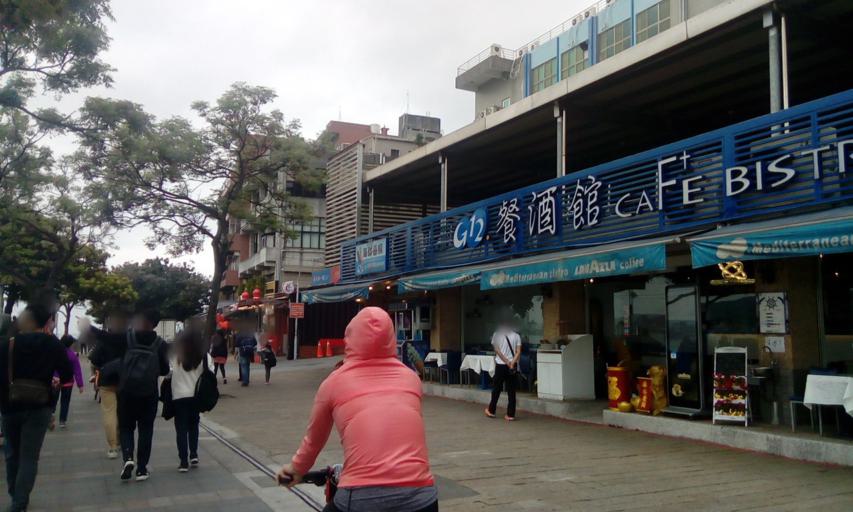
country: TW
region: Taipei
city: Taipei
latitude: 25.1691
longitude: 121.4415
